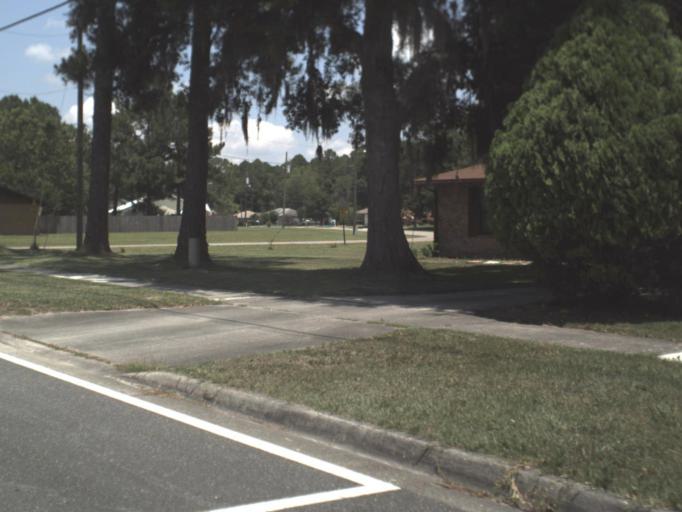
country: US
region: Florida
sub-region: Bradford County
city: Starke
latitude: 29.9568
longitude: -82.1148
